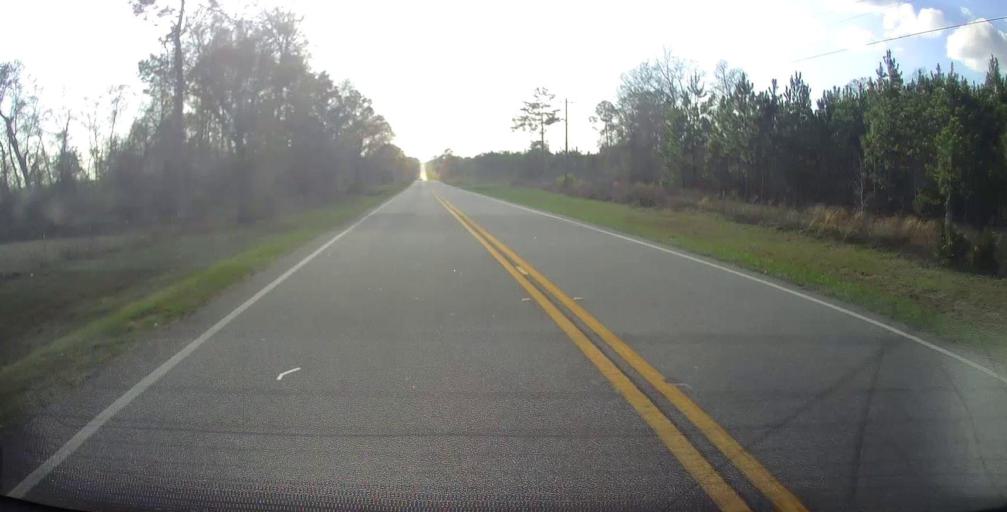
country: US
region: Georgia
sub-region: Wheeler County
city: Alamo
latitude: 32.1627
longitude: -82.7252
